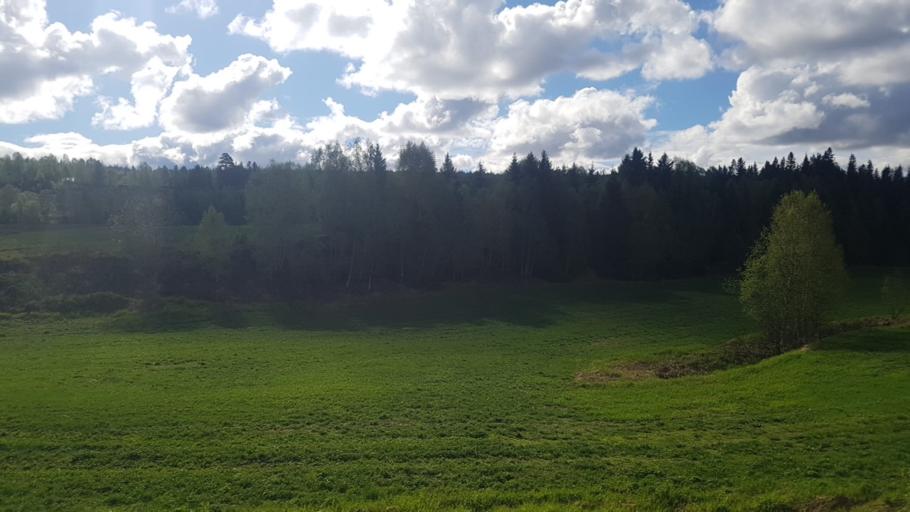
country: NO
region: Sor-Trondelag
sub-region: Rennebu
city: Berkak
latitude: 62.8912
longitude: 10.0966
